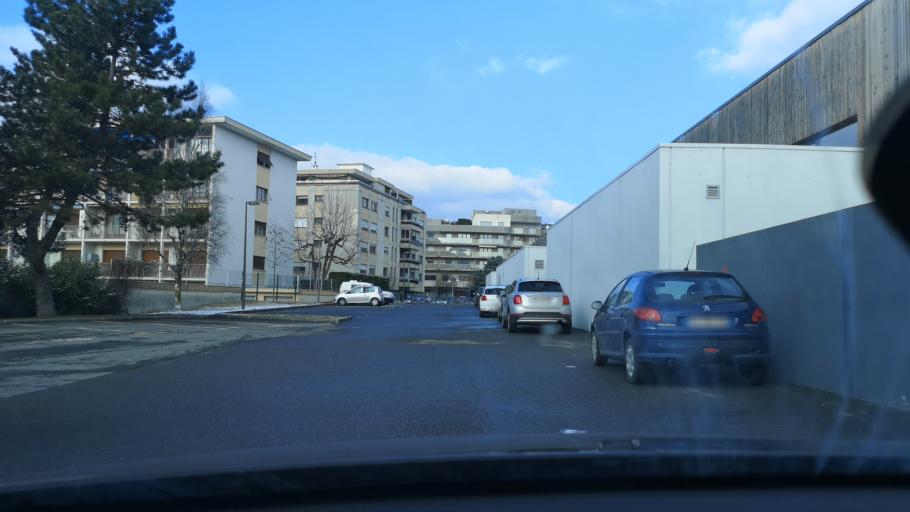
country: FR
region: Rhone-Alpes
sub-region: Departement de la Haute-Savoie
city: Annemasse
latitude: 46.1883
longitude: 6.2340
